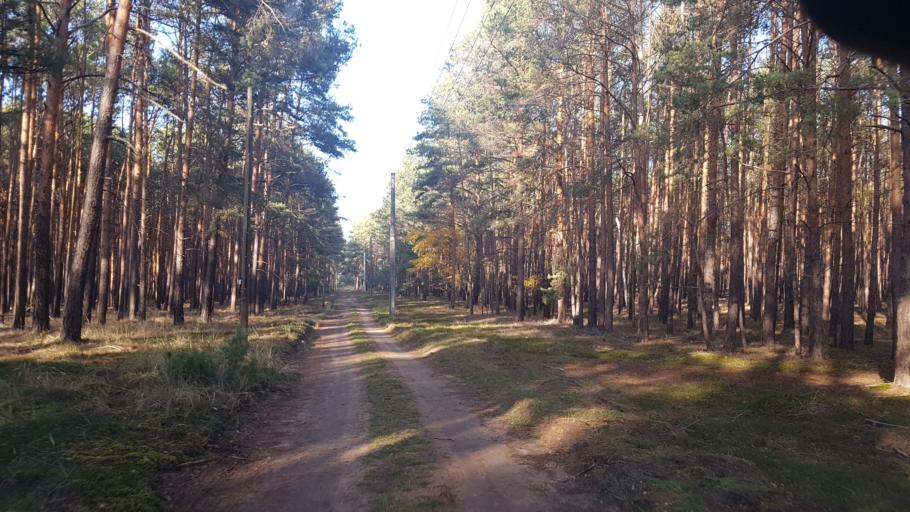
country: DE
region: Brandenburg
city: Schilda
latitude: 51.6431
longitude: 13.3496
